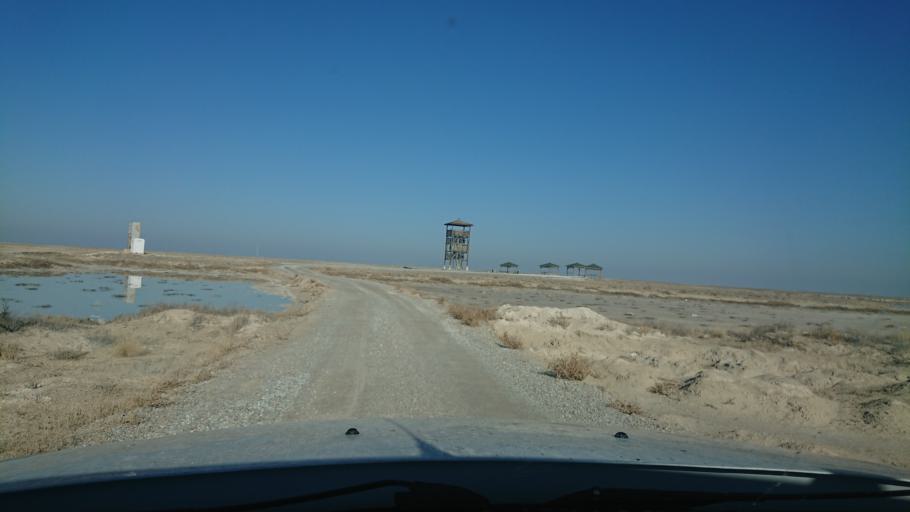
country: TR
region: Aksaray
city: Eskil
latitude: 38.4240
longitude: 33.5008
